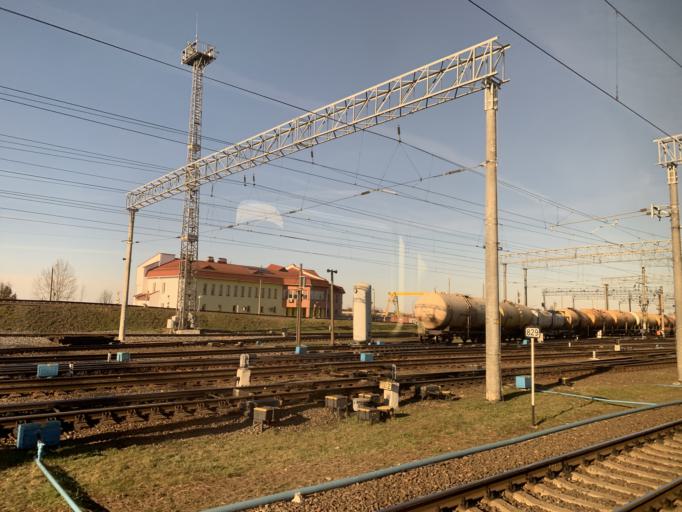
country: BY
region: Minsk
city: Maladzyechna
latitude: 54.3169
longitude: 26.8214
